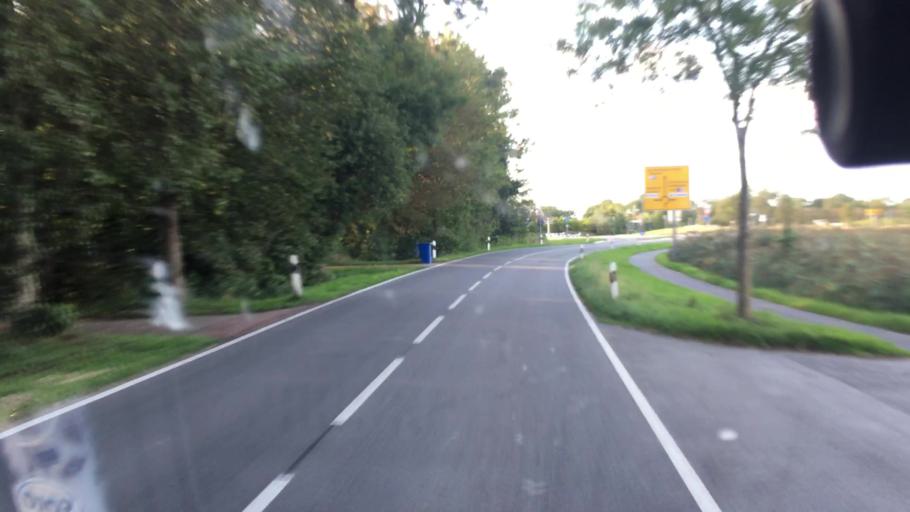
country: DE
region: Lower Saxony
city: Neuharlingersiel
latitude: 53.6885
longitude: 7.6864
